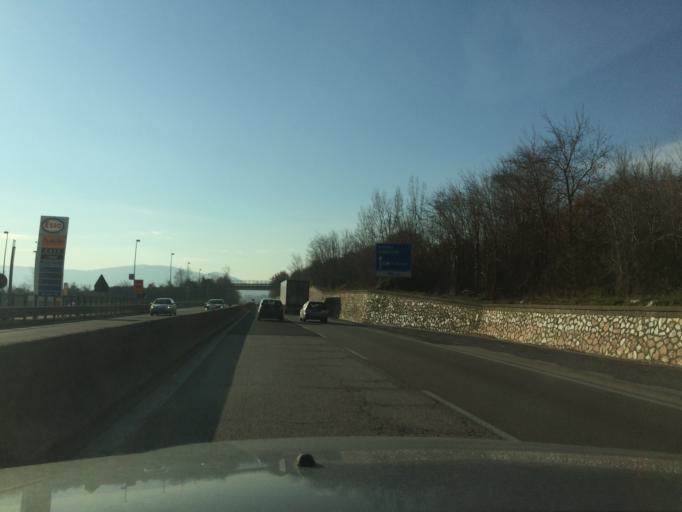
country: IT
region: Umbria
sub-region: Provincia di Terni
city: Narni Scalo
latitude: 42.5629
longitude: 12.5494
